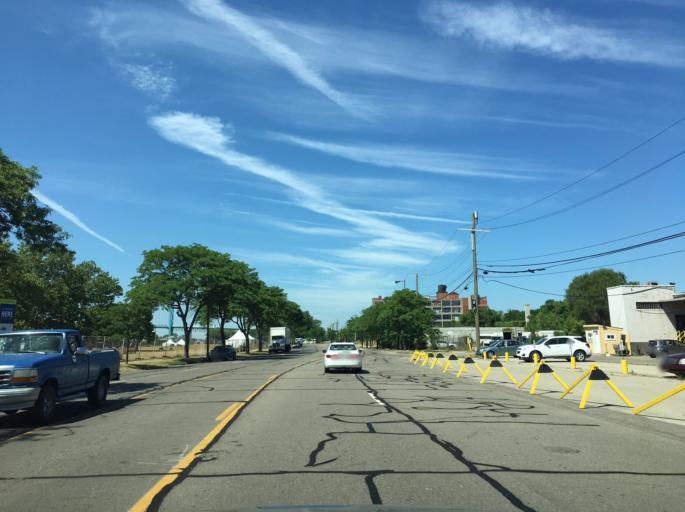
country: US
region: Michigan
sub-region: Wayne County
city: Detroit
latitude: 42.3227
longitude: -83.0625
